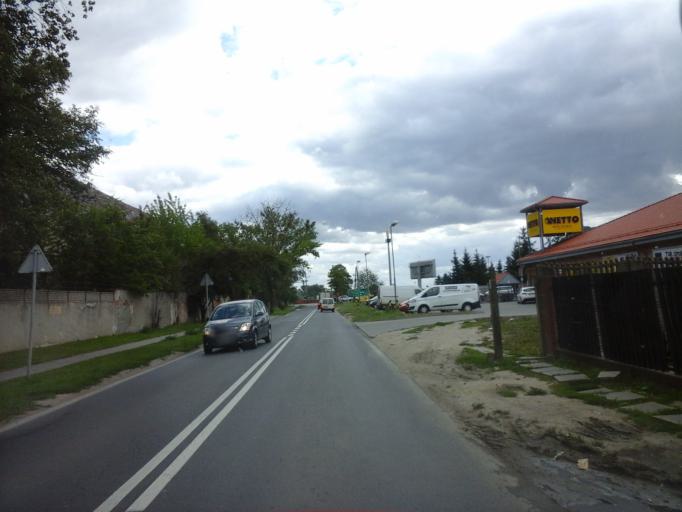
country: PL
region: West Pomeranian Voivodeship
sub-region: Powiat policki
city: Przeclaw
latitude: 53.3919
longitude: 14.4838
